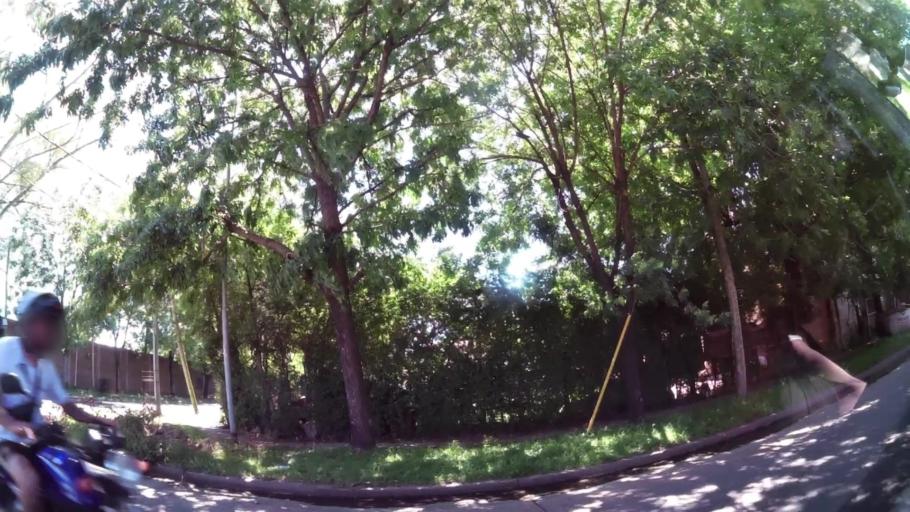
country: AR
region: Buenos Aires
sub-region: Partido de Tigre
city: Tigre
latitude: -34.4960
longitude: -58.6276
